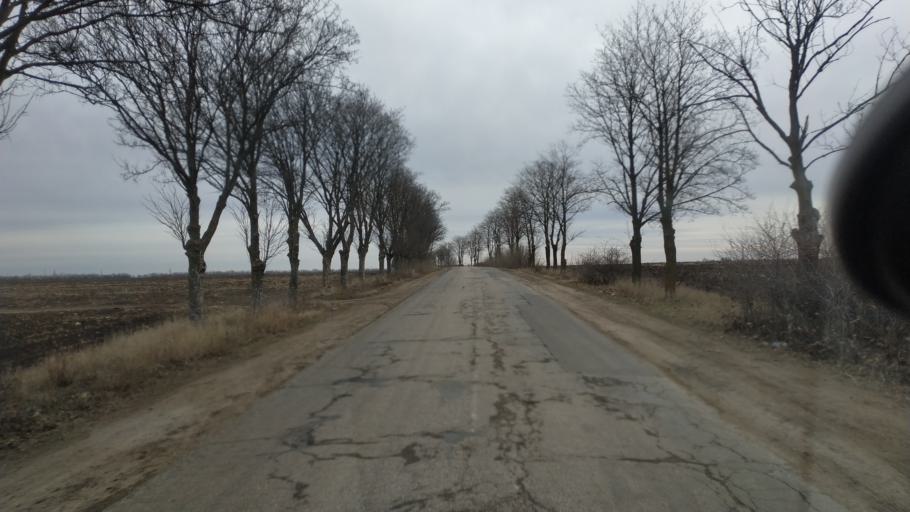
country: MD
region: Telenesti
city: Cocieri
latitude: 47.2661
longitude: 29.0867
